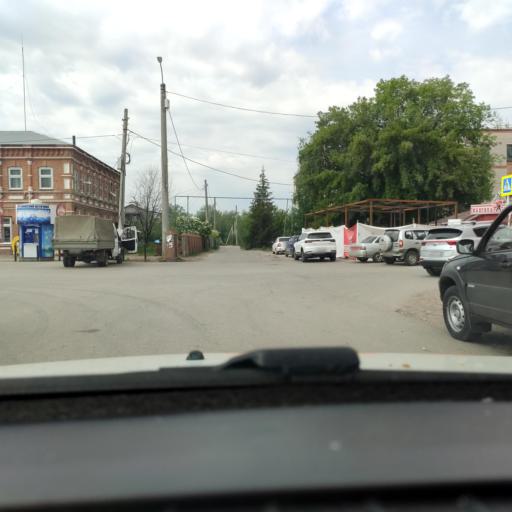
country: RU
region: Samara
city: Krasnyy Yar
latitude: 53.4974
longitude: 50.3868
